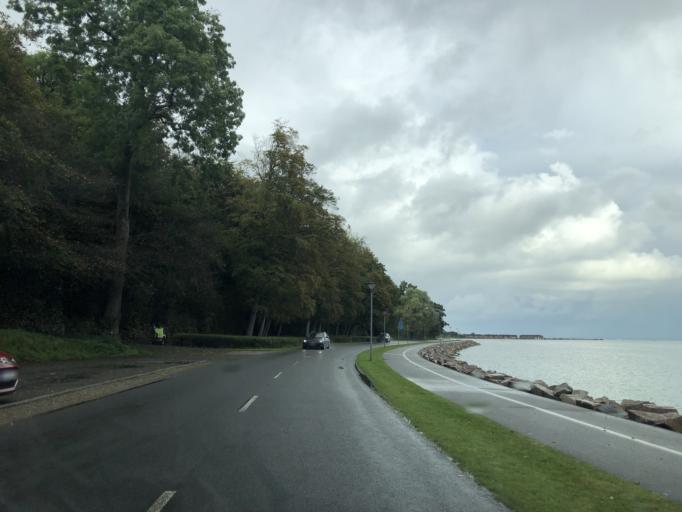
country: DK
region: Central Jutland
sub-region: Lemvig Kommune
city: Lemvig
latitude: 56.5535
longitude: 8.2962
